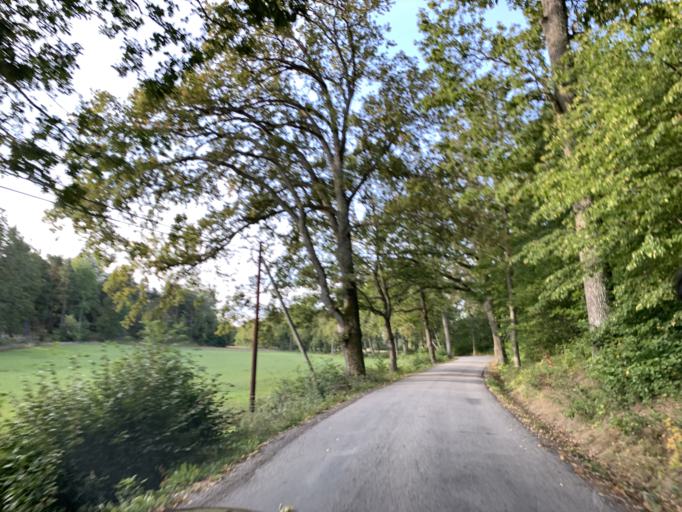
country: SE
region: Stockholm
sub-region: Nynashamns Kommun
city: Osmo
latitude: 59.0459
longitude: 18.0155
